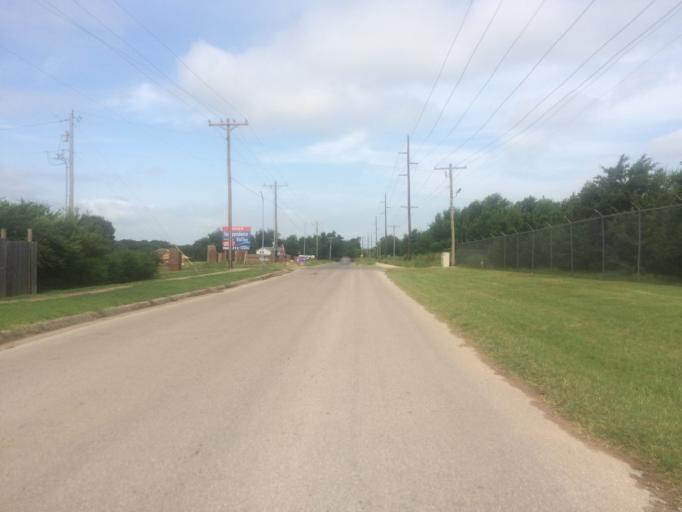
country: US
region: Oklahoma
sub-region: Cleveland County
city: Norman
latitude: 35.1751
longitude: -97.4319
